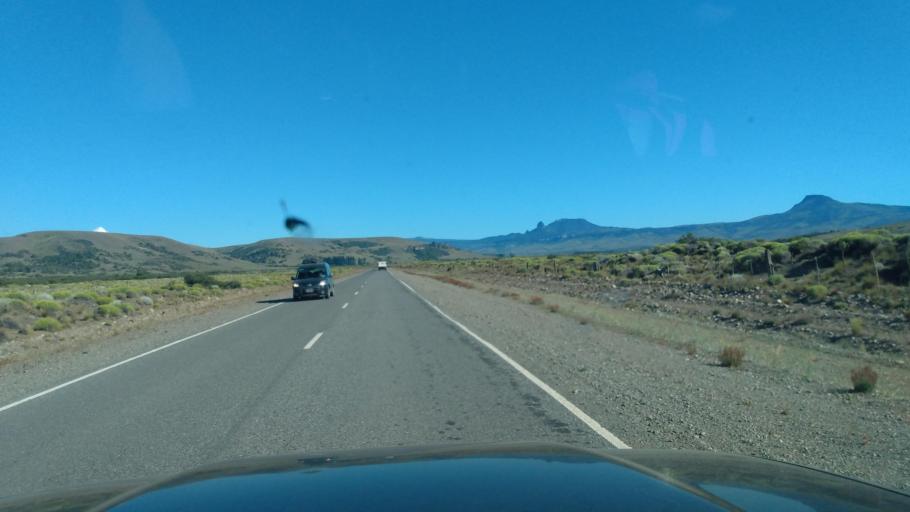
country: AR
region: Neuquen
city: Junin de los Andes
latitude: -39.8701
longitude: -71.1763
